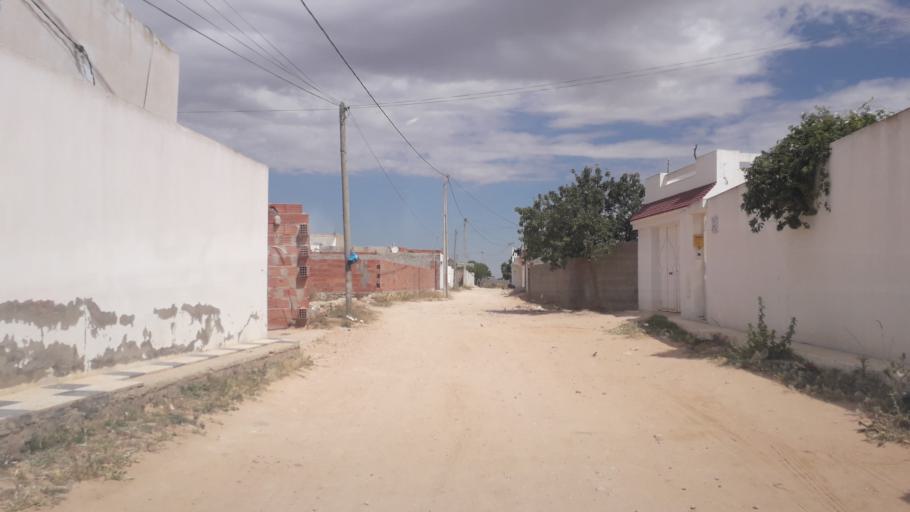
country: TN
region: Safaqis
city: Al Qarmadah
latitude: 34.8418
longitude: 10.7742
